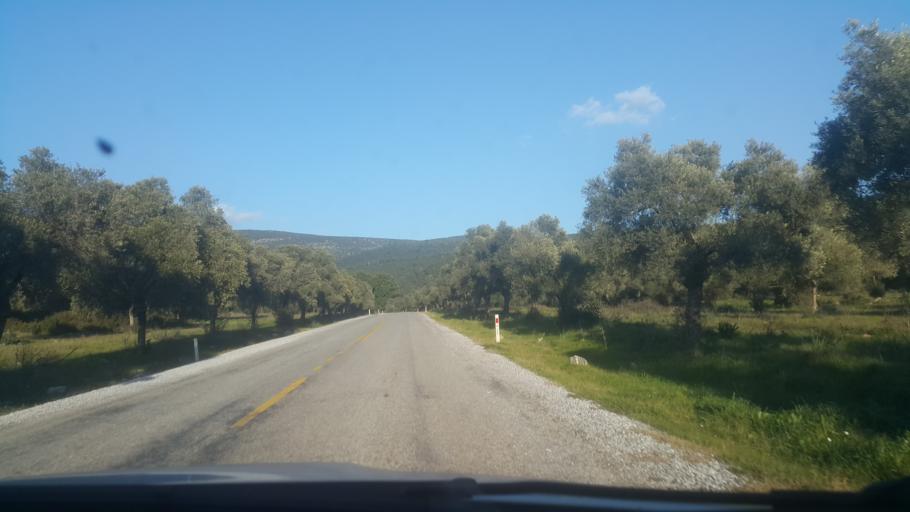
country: TR
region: Mugla
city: Kiulukioi
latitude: 37.3014
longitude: 27.6062
